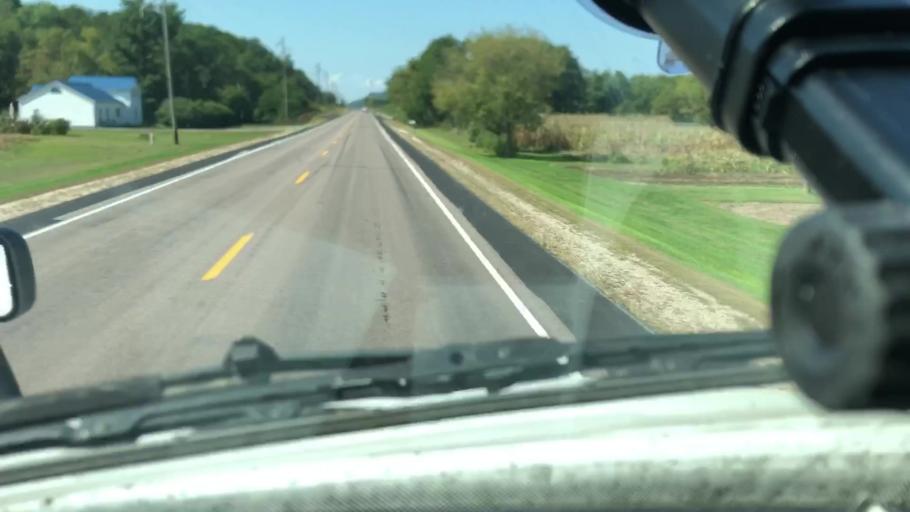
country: US
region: Wisconsin
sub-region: Trempealeau County
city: Trempealeau
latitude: 44.0700
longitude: -91.4985
